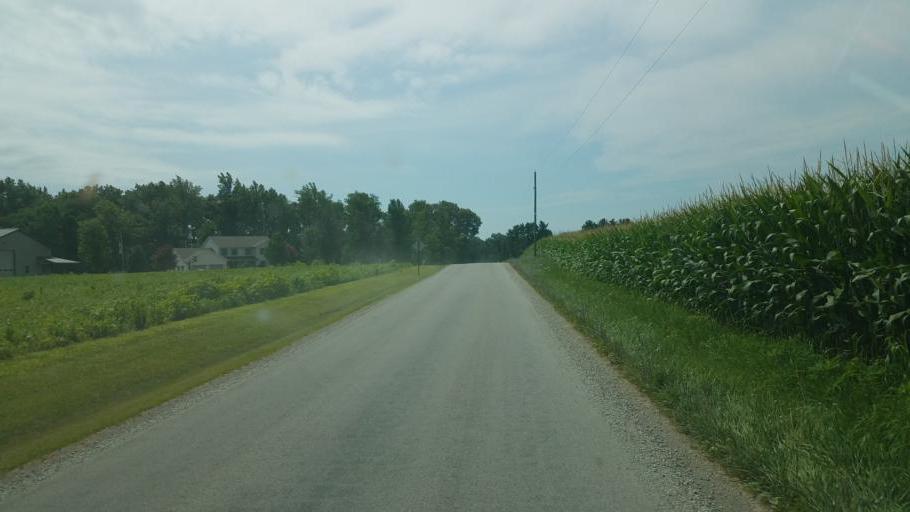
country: US
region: Ohio
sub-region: Wyandot County
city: Upper Sandusky
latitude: 40.8691
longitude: -83.2563
